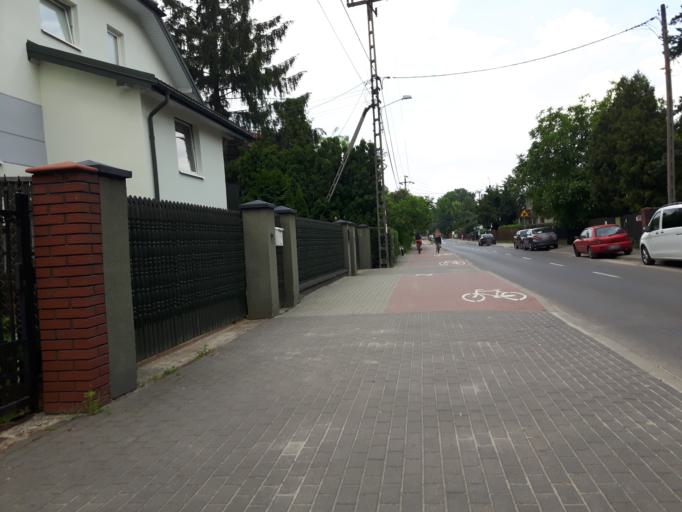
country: PL
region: Masovian Voivodeship
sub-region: Powiat wolominski
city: Zabki
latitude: 52.2917
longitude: 21.1251
